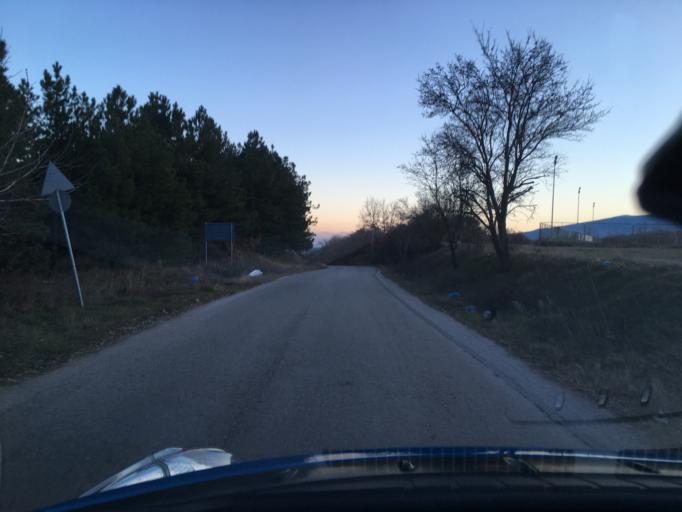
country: GR
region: West Macedonia
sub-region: Nomos Kozanis
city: Kozani
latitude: 40.2657
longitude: 21.7462
